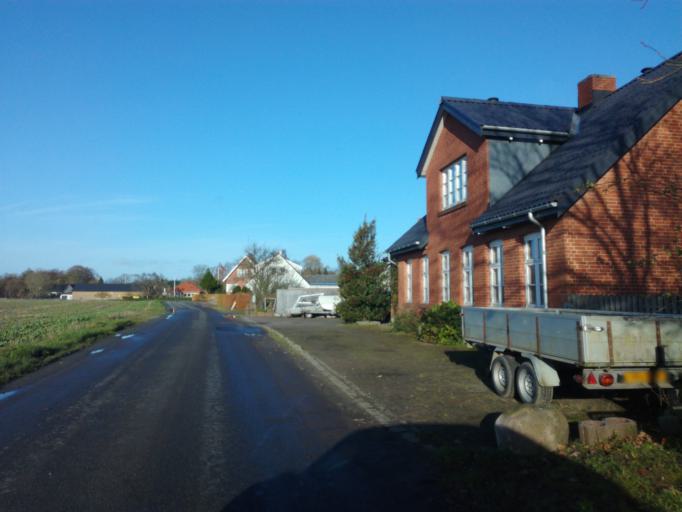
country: DK
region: South Denmark
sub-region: Vejle Kommune
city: Borkop
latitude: 55.6141
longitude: 9.6718
